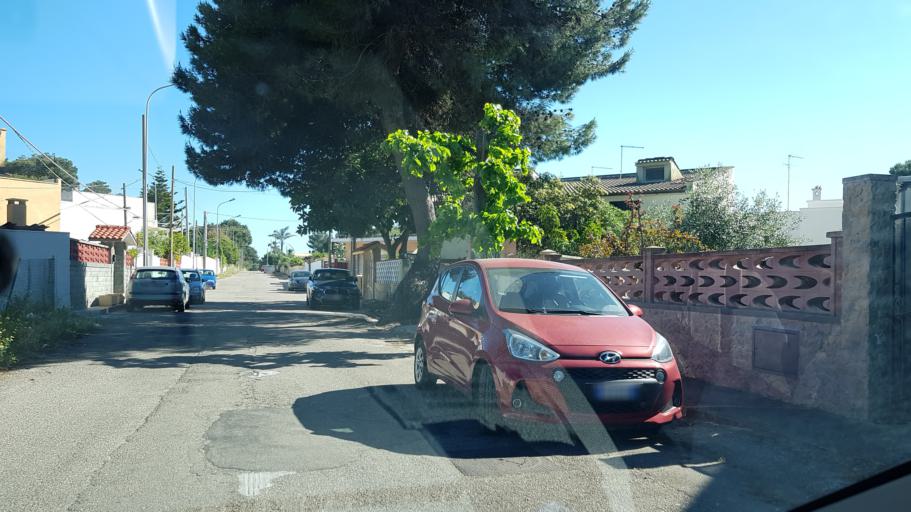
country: IT
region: Apulia
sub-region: Provincia di Brindisi
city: Torchiarolo
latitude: 40.5278
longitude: 18.0754
